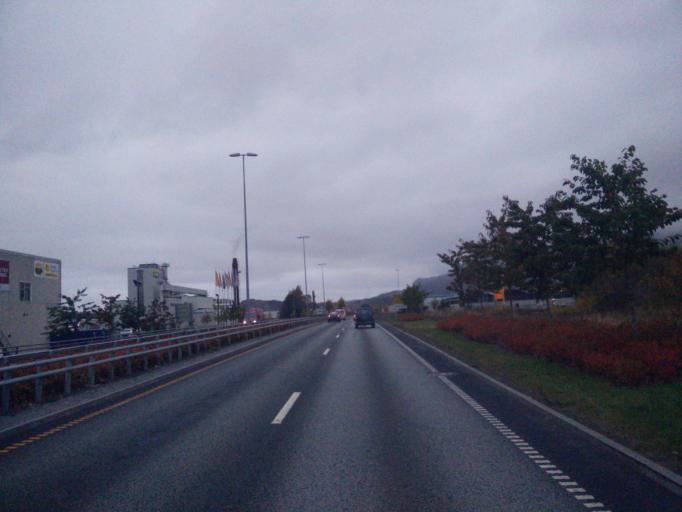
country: NO
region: Nord-Trondelag
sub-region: Stjordal
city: Stjordal
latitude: 63.4737
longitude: 10.9060
